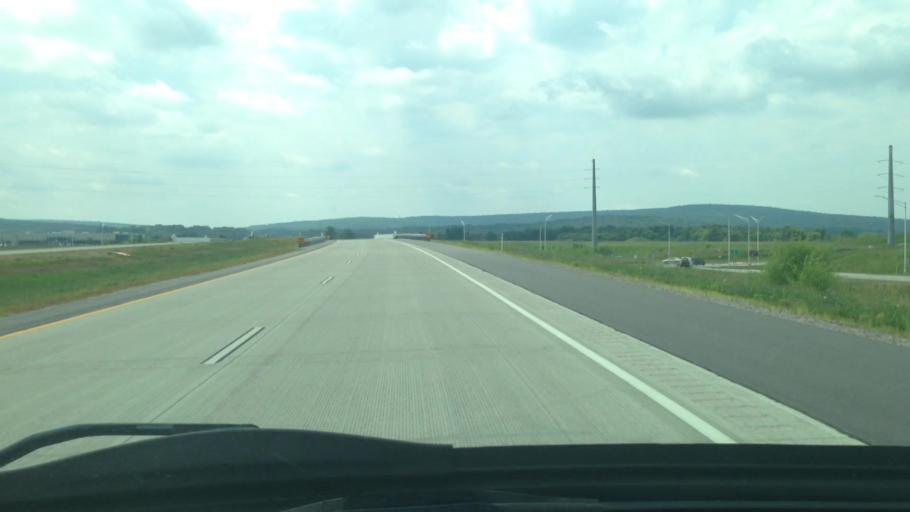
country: US
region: Wisconsin
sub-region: Sauk County
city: West Baraboo
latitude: 43.4620
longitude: -89.7780
